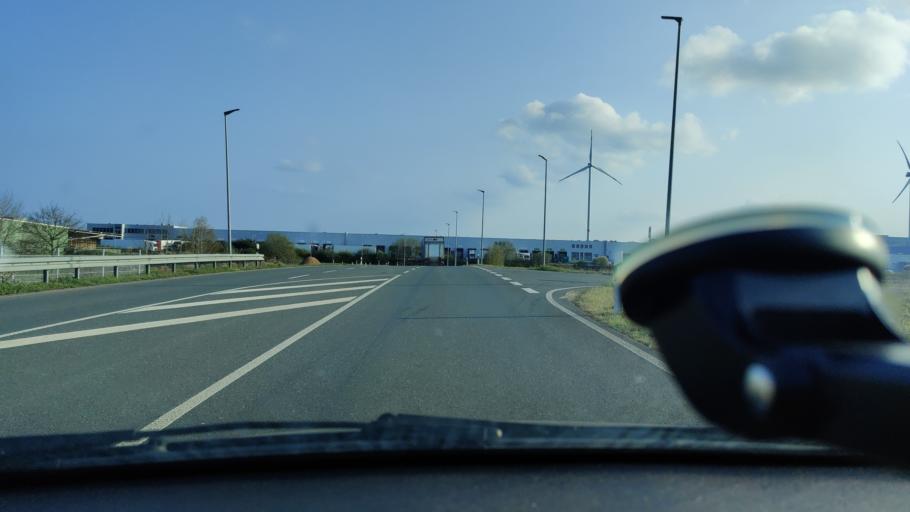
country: DE
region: North Rhine-Westphalia
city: Straelen
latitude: 51.3864
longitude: 6.2375
